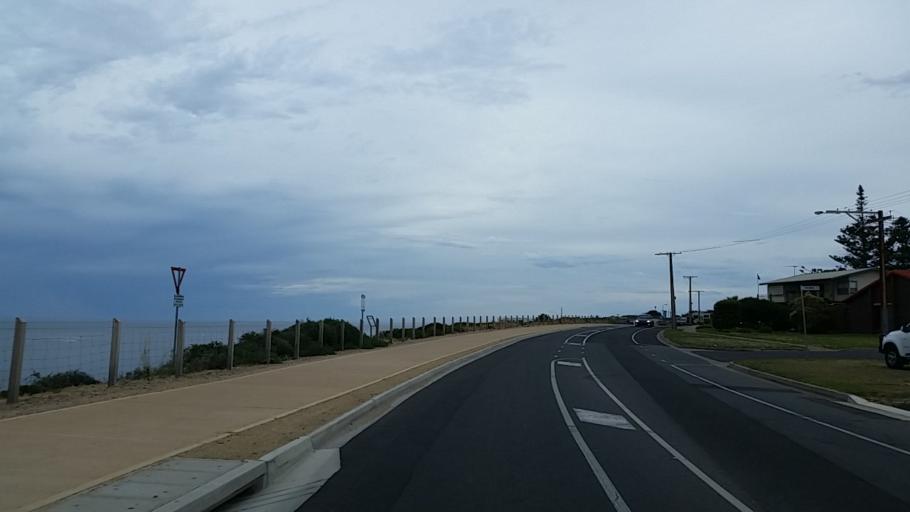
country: AU
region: South Australia
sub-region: Onkaparinga
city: Port Willunga
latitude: -35.2837
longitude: 138.4434
